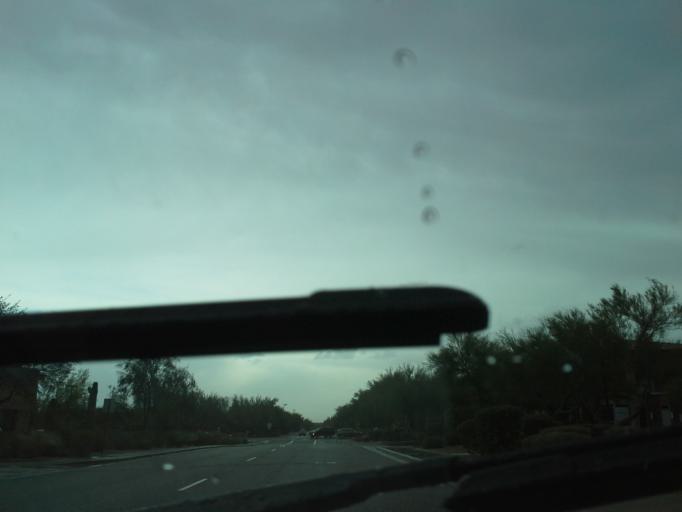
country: US
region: Arizona
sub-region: Maricopa County
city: Paradise Valley
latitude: 33.6382
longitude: -111.8871
